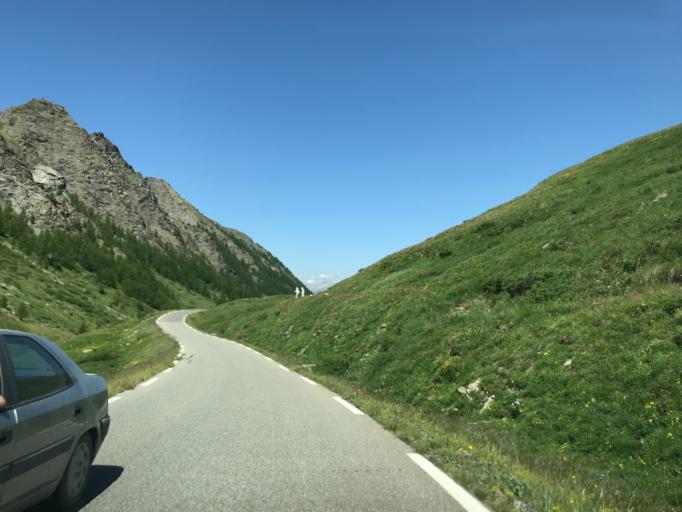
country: IT
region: Piedmont
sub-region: Provincia di Cuneo
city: Pontechianale
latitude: 44.6997
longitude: 6.9435
